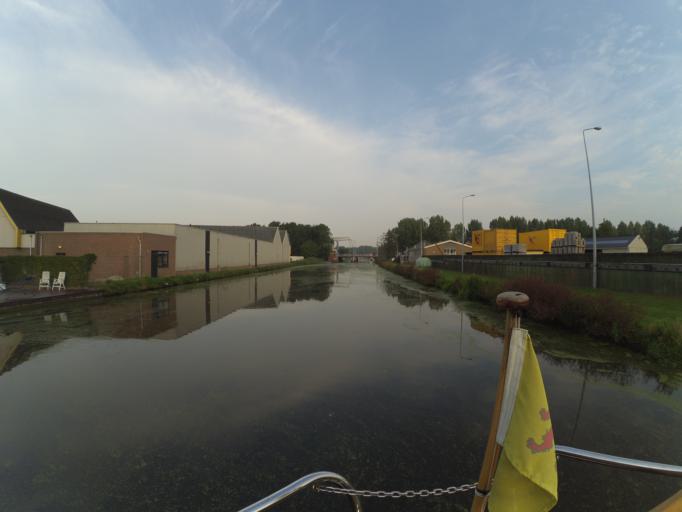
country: NL
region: South Holland
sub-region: Gemeente Vlist
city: Haastrecht
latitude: 52.0036
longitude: 4.7438
